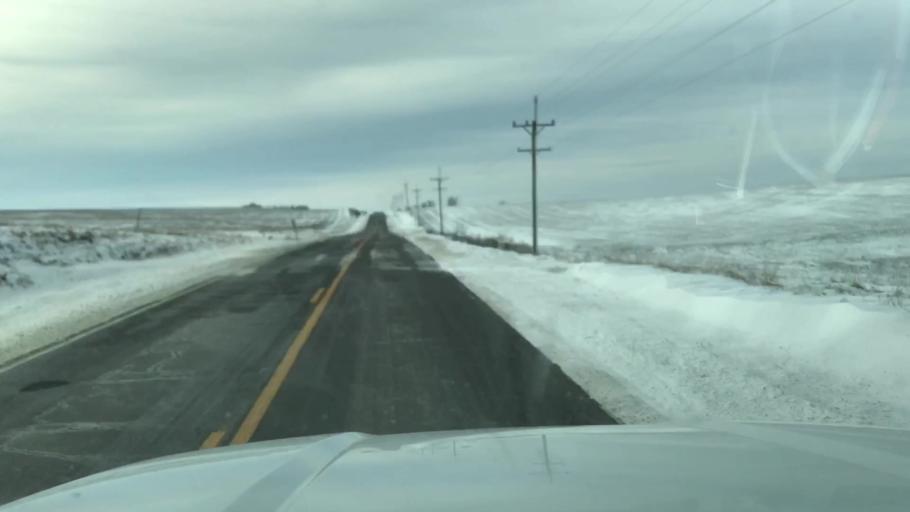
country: US
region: Missouri
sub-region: Holt County
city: Mound City
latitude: 40.1091
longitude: -95.1449
